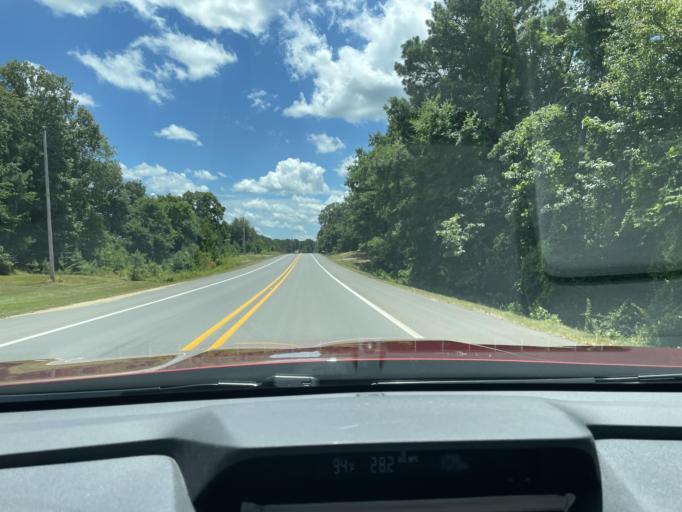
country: US
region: Arkansas
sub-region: Drew County
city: Monticello
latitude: 33.7281
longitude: -91.8128
